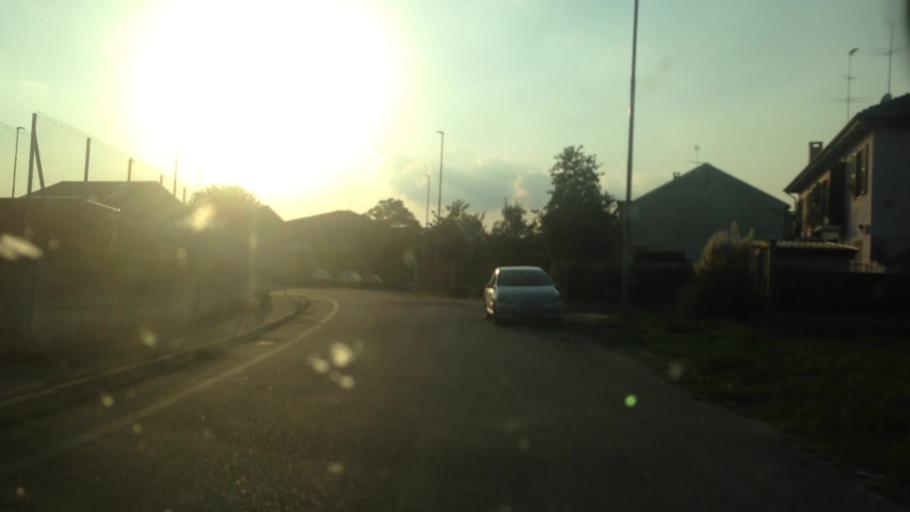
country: IT
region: Piedmont
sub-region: Provincia di Asti
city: Asti
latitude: 44.9163
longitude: 8.2273
